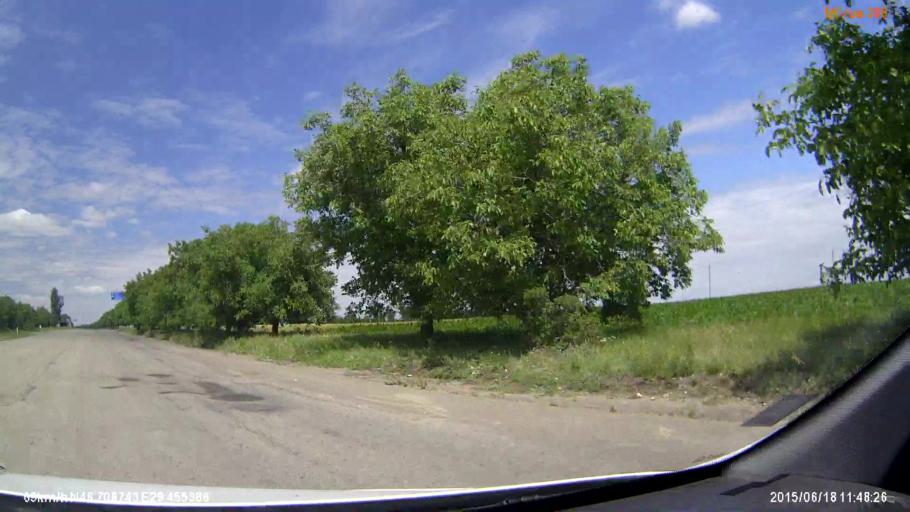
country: MD
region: Causeni
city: Causeni
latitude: 46.7084
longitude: 29.4554
